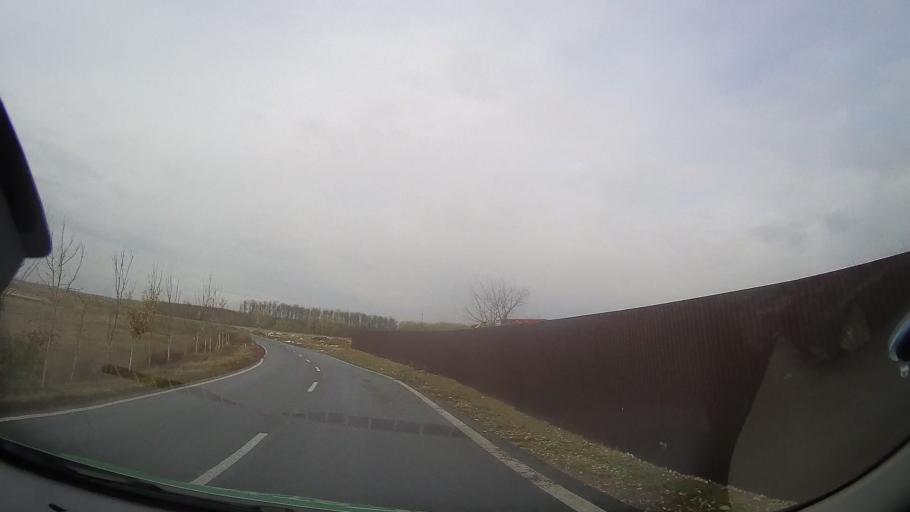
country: RO
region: Ialomita
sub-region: Comuna Fierbinti-Targ
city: Fierbinti-Targ
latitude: 44.6742
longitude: 26.3505
